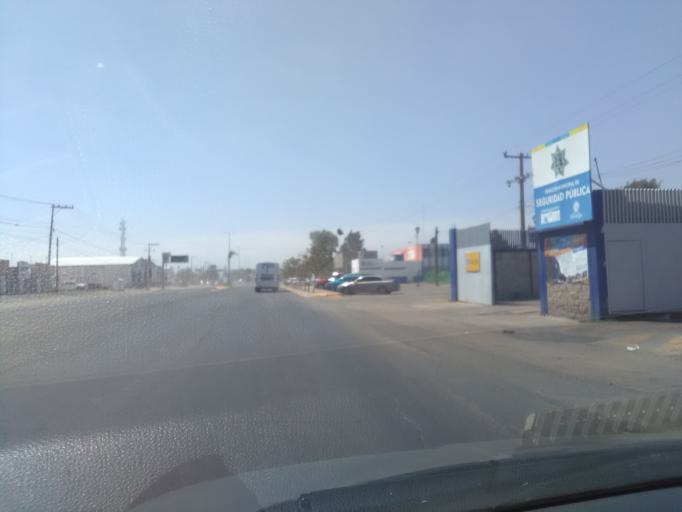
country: MX
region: Durango
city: Victoria de Durango
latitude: 24.0301
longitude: -104.6096
